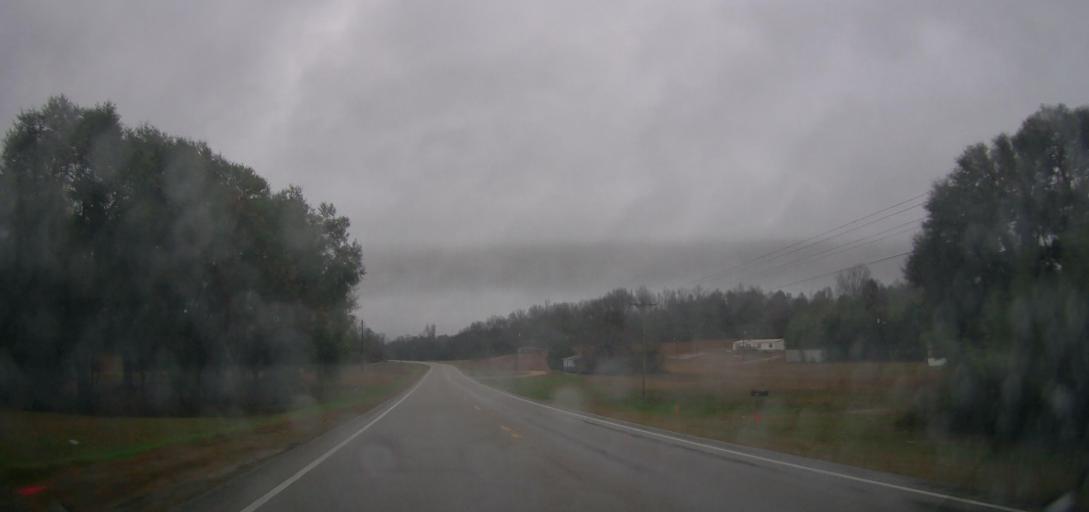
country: US
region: Alabama
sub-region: Autauga County
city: Pine Level
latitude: 32.5255
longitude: -86.6284
